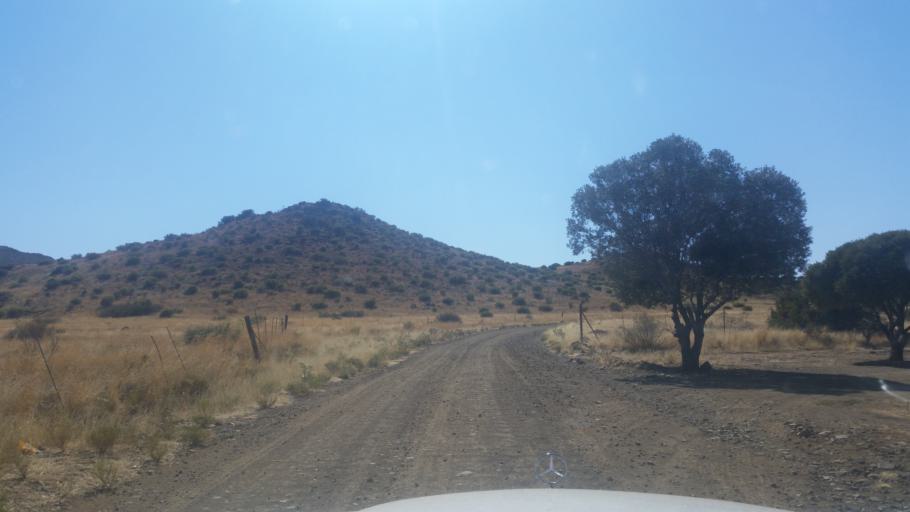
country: ZA
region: Orange Free State
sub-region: Xhariep District Municipality
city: Trompsburg
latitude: -30.4845
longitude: 25.9991
